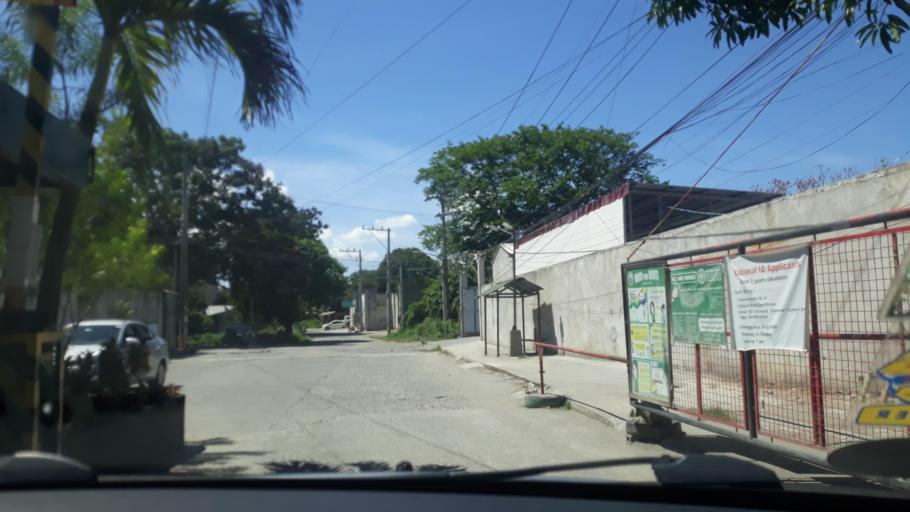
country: PH
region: Calabarzon
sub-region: Province of Cavite
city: Manggahan
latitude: 14.2977
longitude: 120.9175
